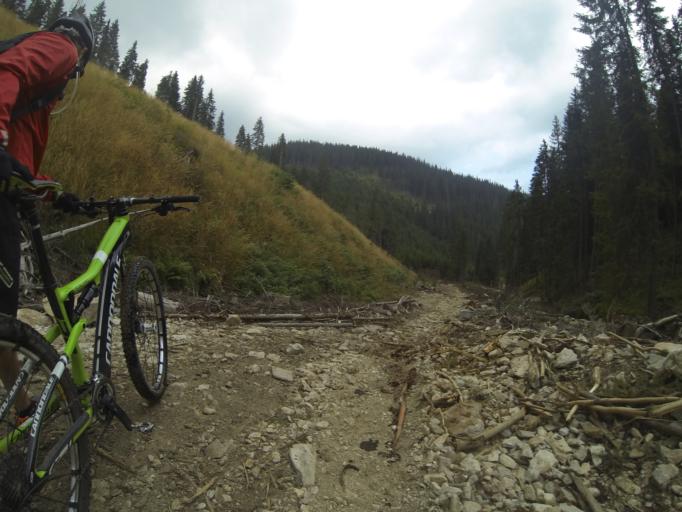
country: RO
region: Gorj
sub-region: Comuna Polovragi
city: Polovragi
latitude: 45.2960
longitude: 23.8465
